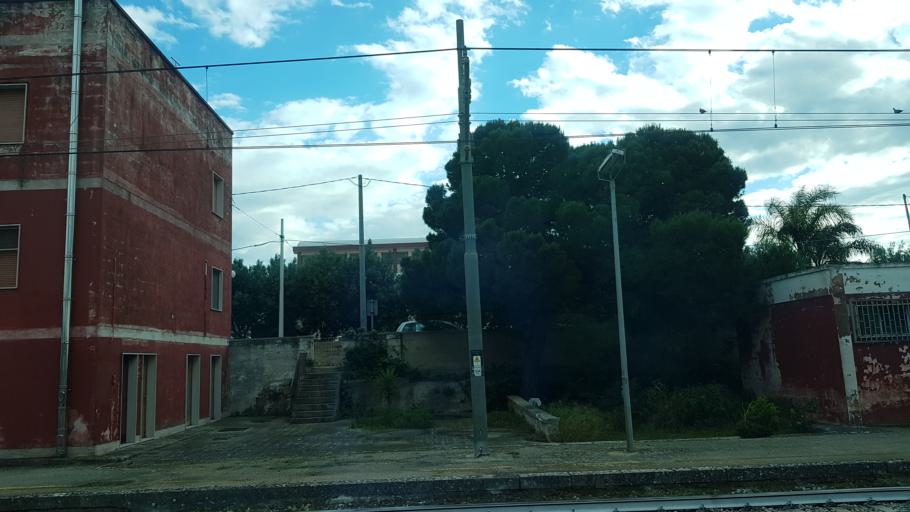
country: IT
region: Apulia
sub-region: Provincia di Brindisi
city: Montalbano
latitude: 40.8161
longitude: 17.4579
